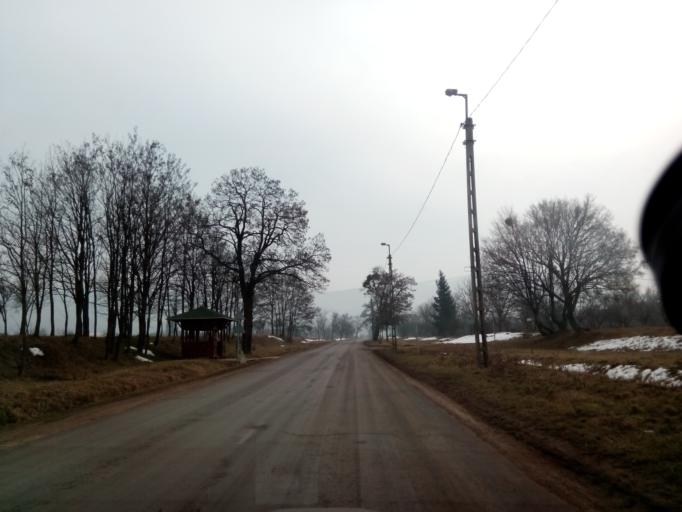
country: HU
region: Borsod-Abauj-Zemplen
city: Gonc
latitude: 48.4775
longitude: 21.2635
